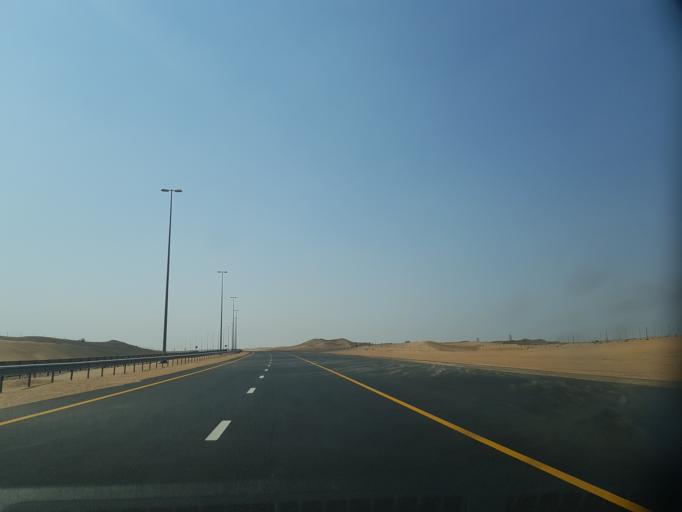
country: AE
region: Ash Shariqah
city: Adh Dhayd
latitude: 25.2695
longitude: 55.6519
